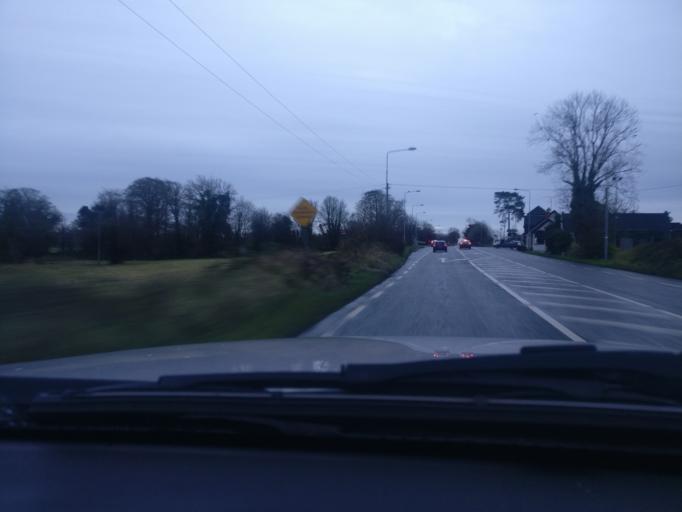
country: IE
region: Leinster
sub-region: An Mhi
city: Navan
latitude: 53.6872
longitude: -6.7699
